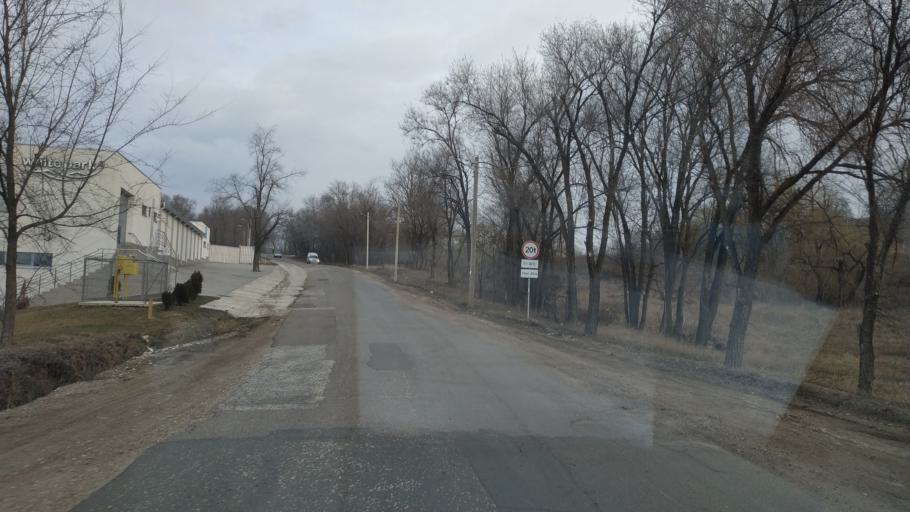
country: MD
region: Chisinau
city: Singera
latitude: 46.9269
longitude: 29.0490
